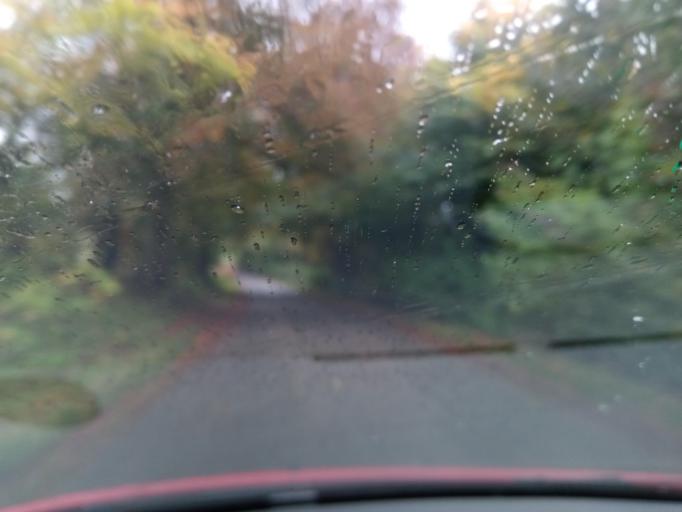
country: GB
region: Scotland
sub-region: The Scottish Borders
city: Selkirk
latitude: 55.5119
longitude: -2.7728
